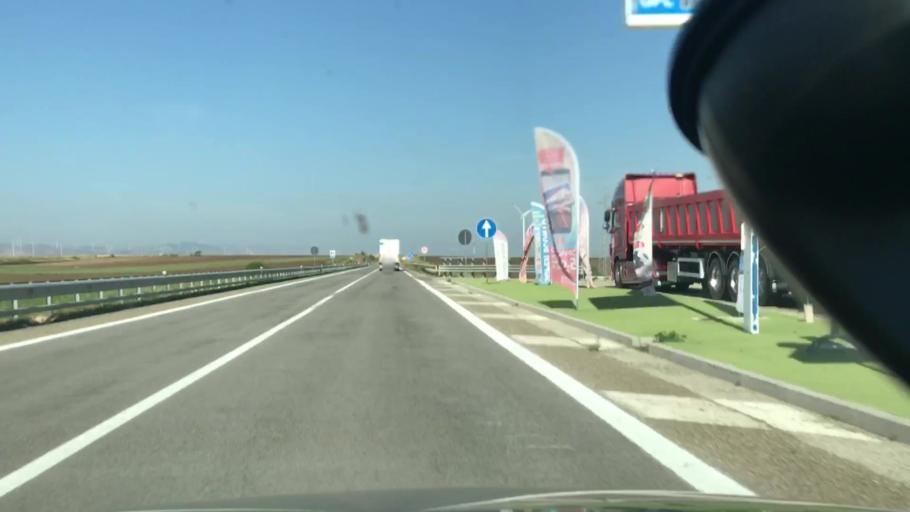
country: IT
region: Basilicate
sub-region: Provincia di Potenza
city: Lavello
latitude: 41.0175
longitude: 15.8159
